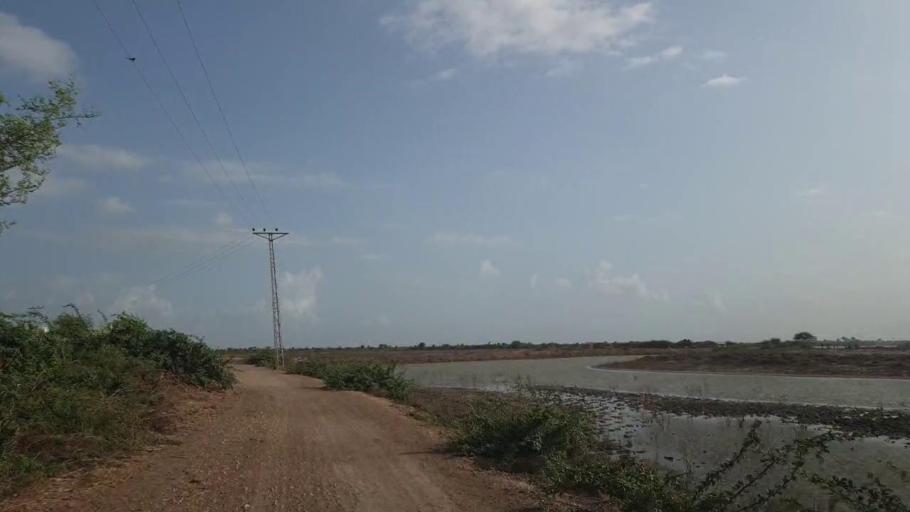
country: PK
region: Sindh
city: Kadhan
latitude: 24.6330
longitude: 69.0805
